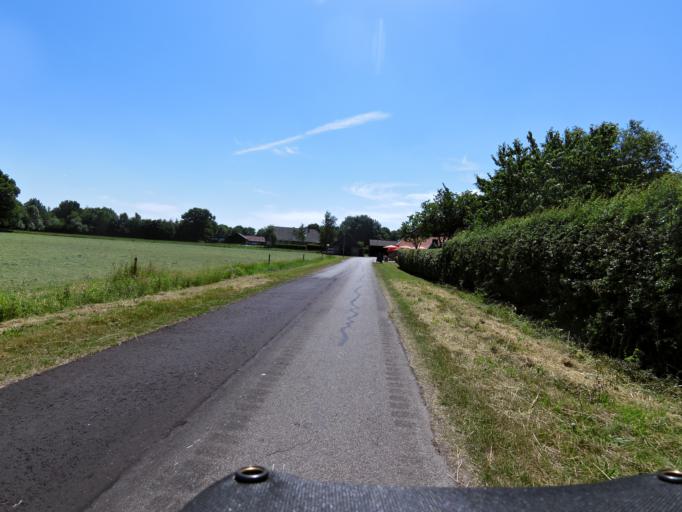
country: NL
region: Overijssel
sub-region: Gemeente Twenterand
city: Den Ham
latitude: 52.4957
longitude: 6.4037
